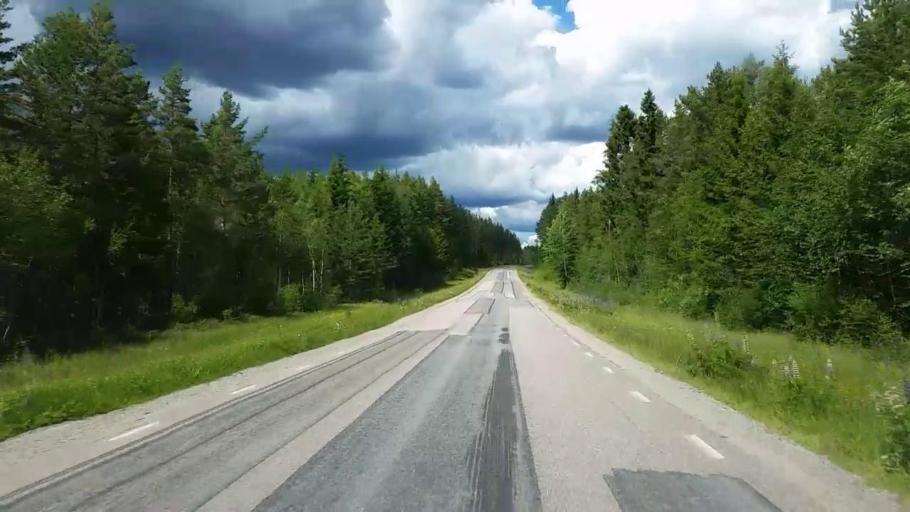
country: SE
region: Gaevleborg
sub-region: Ovanakers Kommun
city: Edsbyn
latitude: 61.3993
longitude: 15.8964
